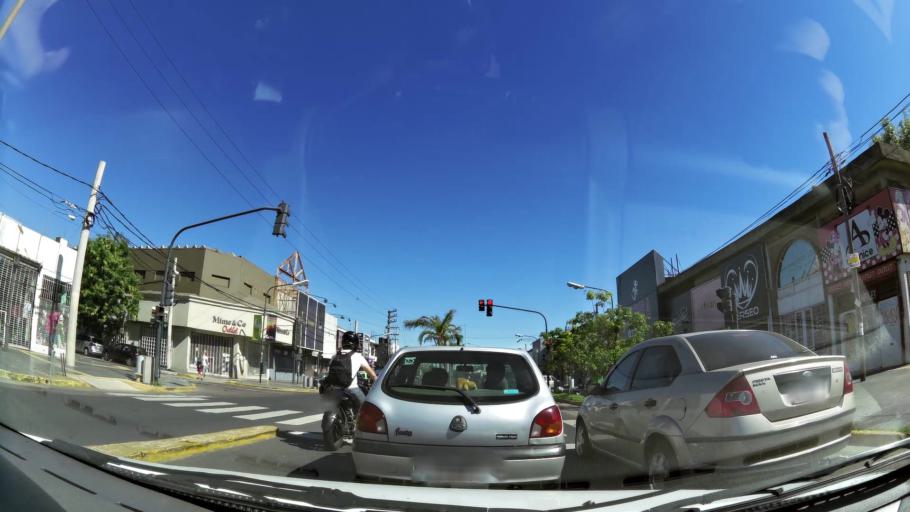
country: AR
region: Buenos Aires
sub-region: Partido de Vicente Lopez
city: Olivos
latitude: -34.5279
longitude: -58.5172
